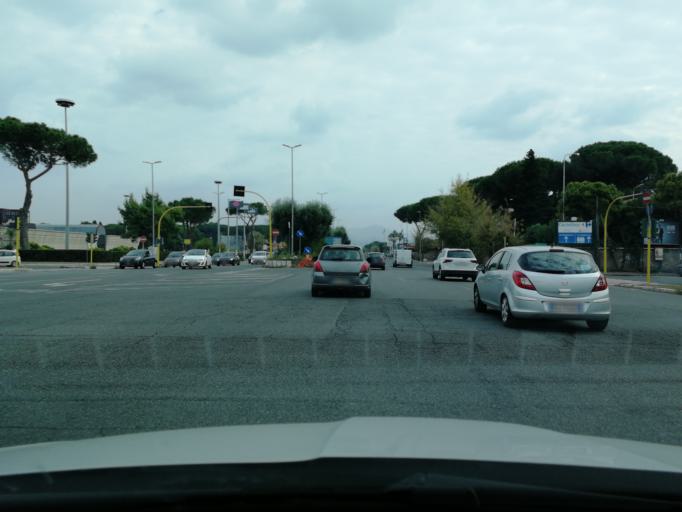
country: IT
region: Latium
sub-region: Citta metropolitana di Roma Capitale
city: Ciampino
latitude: 41.8526
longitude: 12.5695
